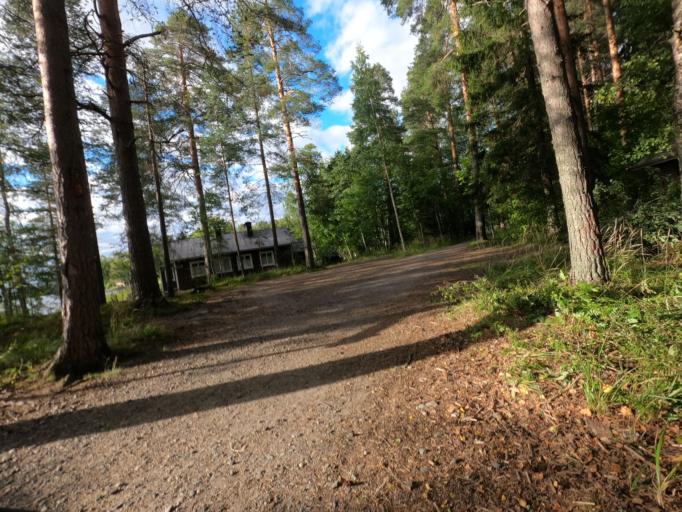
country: FI
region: North Karelia
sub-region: Joensuu
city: Joensuu
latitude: 62.6013
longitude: 29.7207
